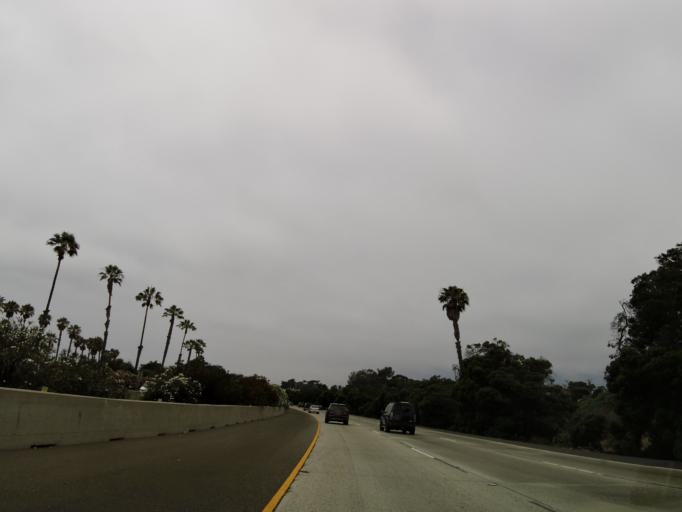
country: US
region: California
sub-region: Ventura County
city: Ventura
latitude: 34.2711
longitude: -119.2750
